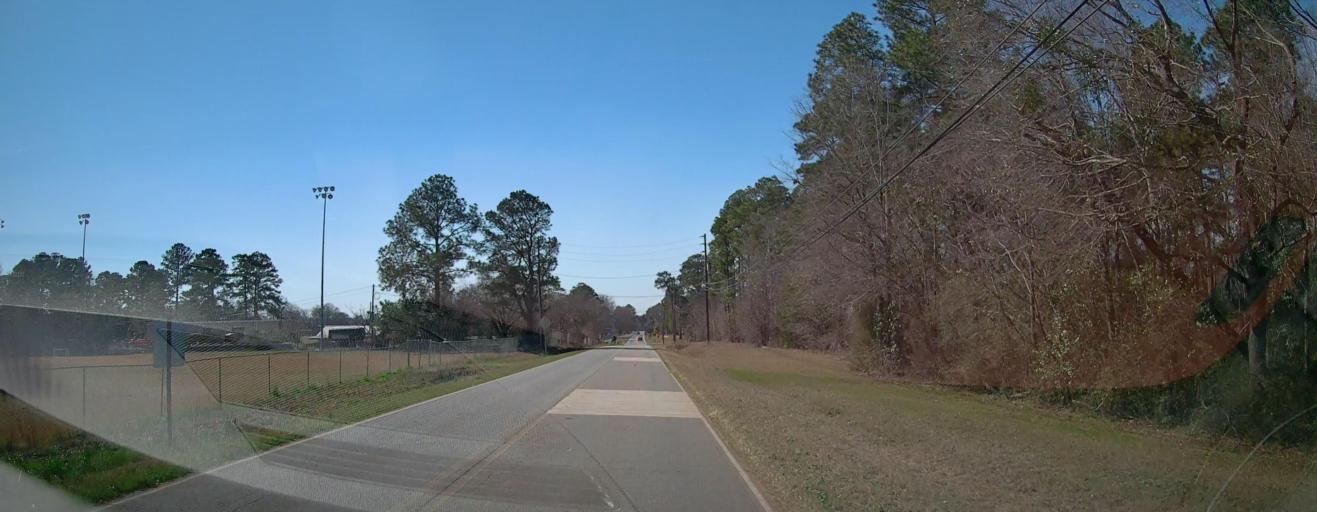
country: US
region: Georgia
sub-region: Houston County
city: Perry
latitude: 32.4659
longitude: -83.7056
